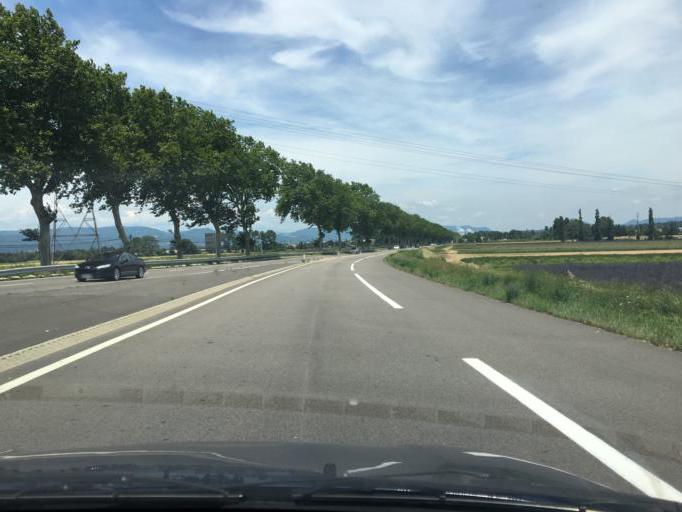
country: FR
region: Rhone-Alpes
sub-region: Departement de la Drome
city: Malataverne
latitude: 44.4976
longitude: 4.7437
